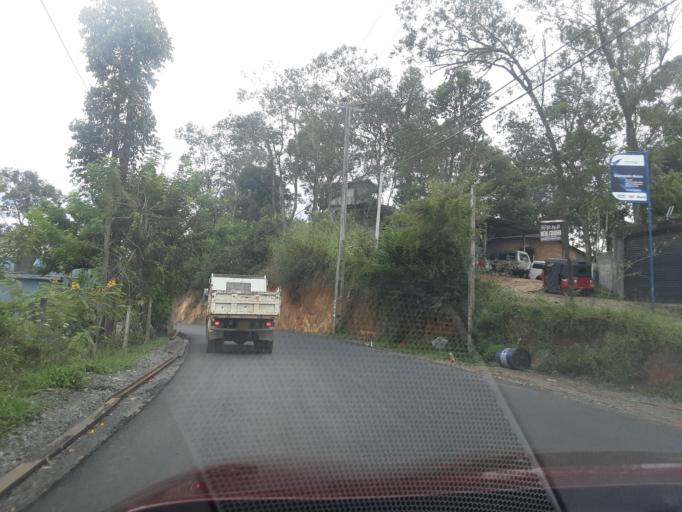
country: LK
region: Uva
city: Haputale
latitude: 6.8363
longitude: 80.9999
